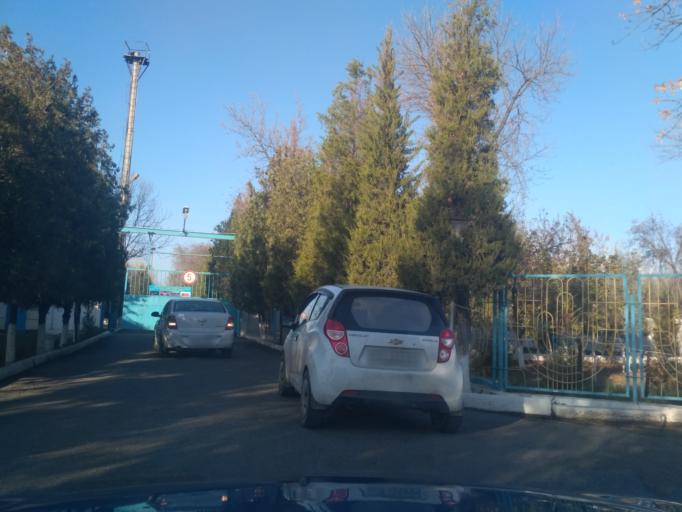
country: UZ
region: Sirdaryo
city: Guliston
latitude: 40.4891
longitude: 68.7473
